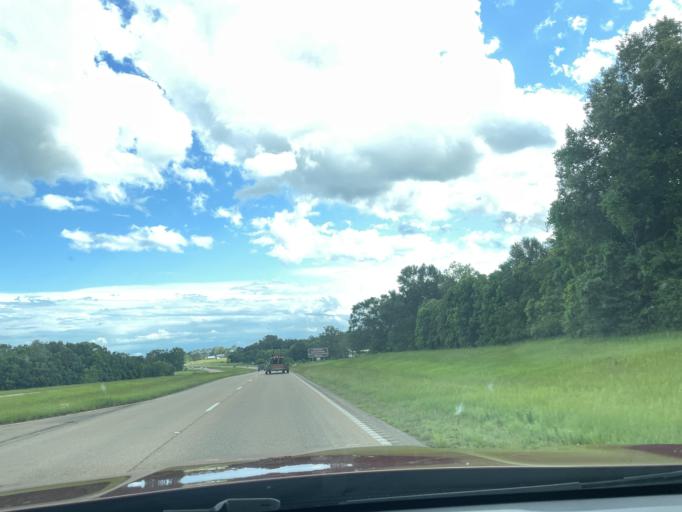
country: US
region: Mississippi
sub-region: Madison County
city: Flora
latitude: 32.5464
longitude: -90.3215
